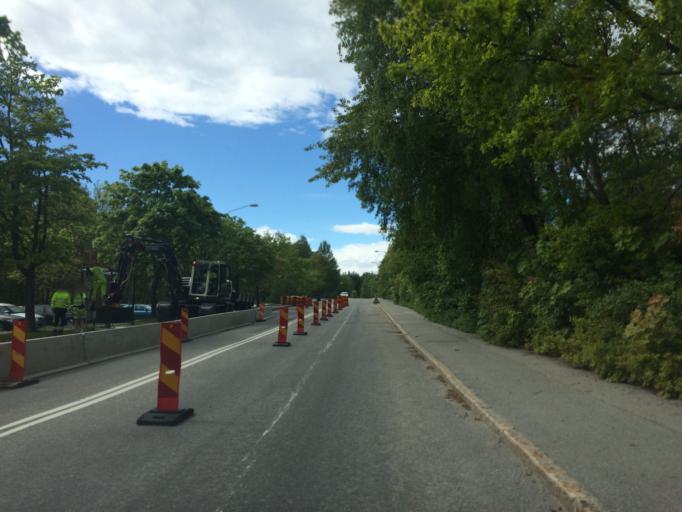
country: SE
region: Stockholm
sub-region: Botkyrka Kommun
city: Fittja
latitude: 59.2724
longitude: 17.8860
